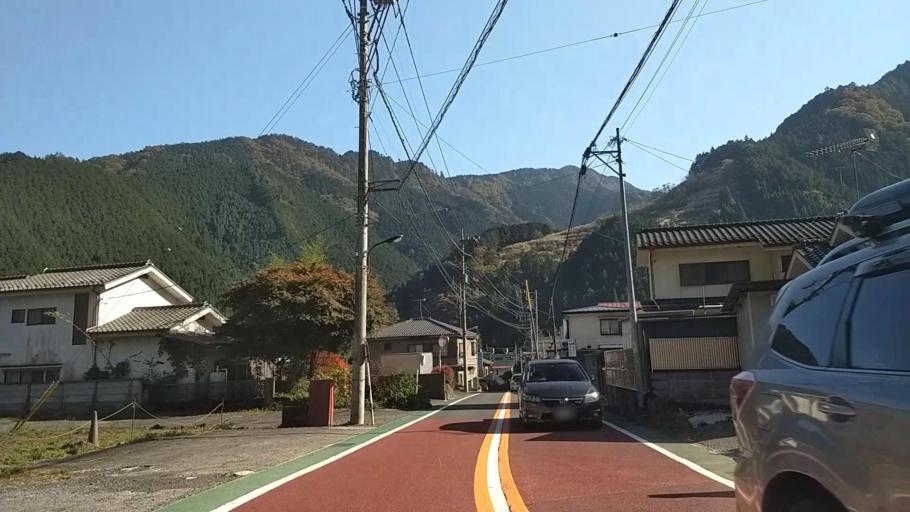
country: JP
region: Tokyo
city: Itsukaichi
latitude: 35.8016
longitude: 139.0877
